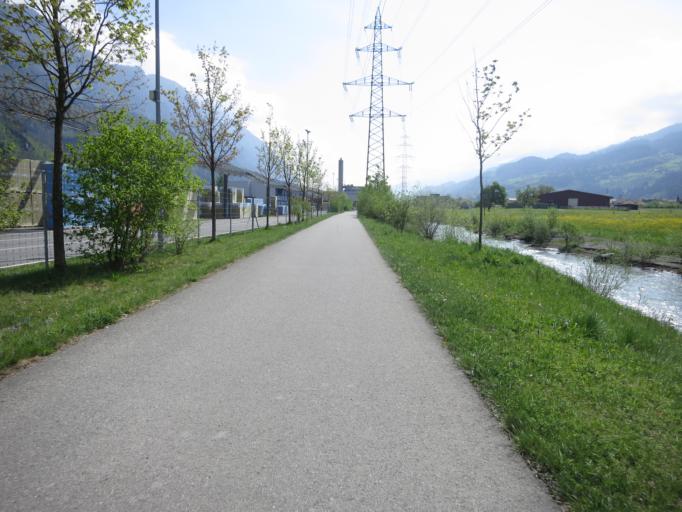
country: CH
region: Saint Gallen
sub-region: Wahlkreis Sarganserland
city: Flums
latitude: 47.1022
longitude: 9.3391
